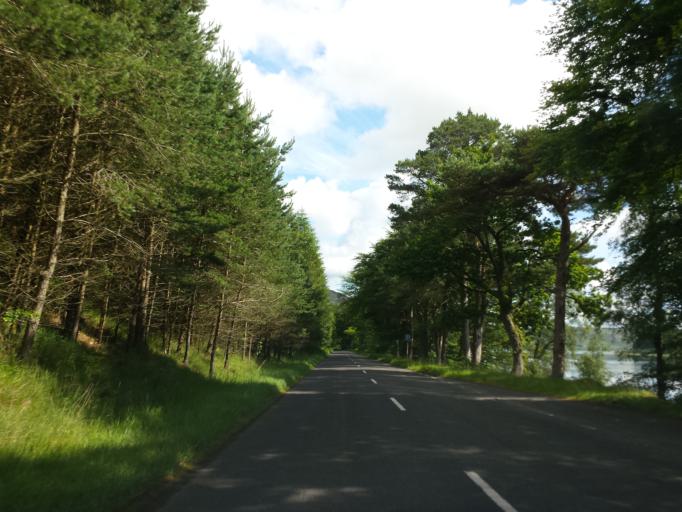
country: GB
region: Scotland
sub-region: The Scottish Borders
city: Peebles
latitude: 55.4806
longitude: -3.2081
